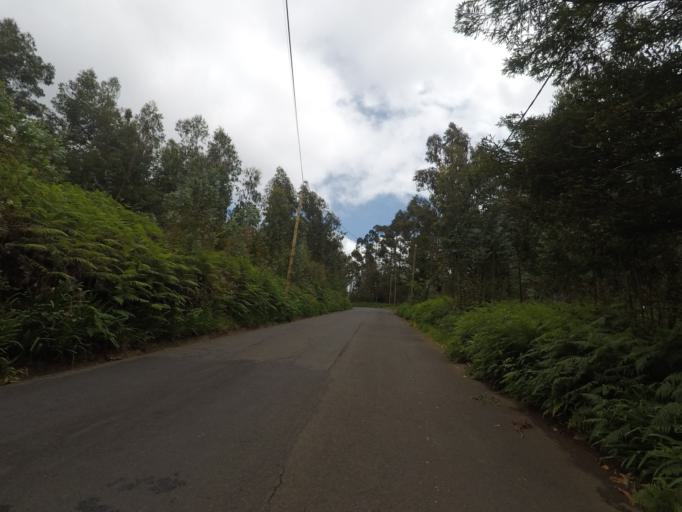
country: PT
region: Madeira
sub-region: Calheta
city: Estreito da Calheta
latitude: 32.7499
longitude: -17.1944
